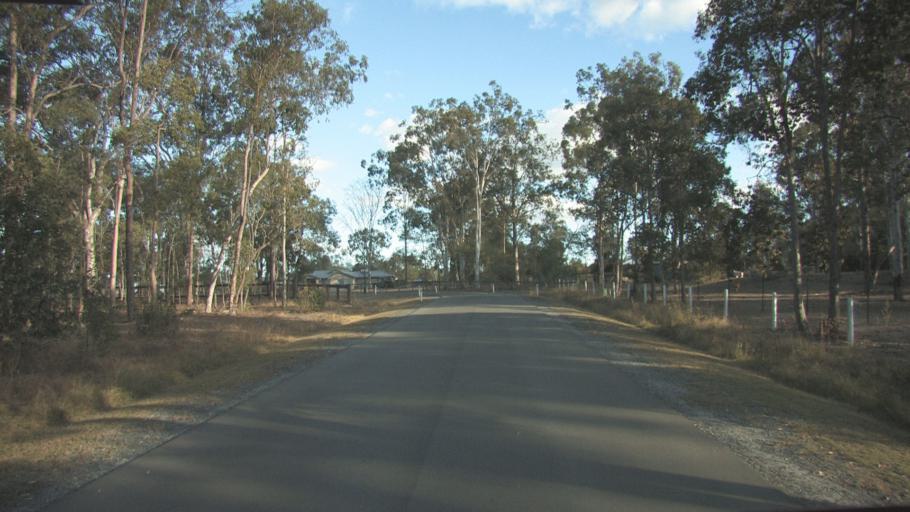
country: AU
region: Queensland
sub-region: Logan
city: Cedar Vale
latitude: -27.8582
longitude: 153.0923
